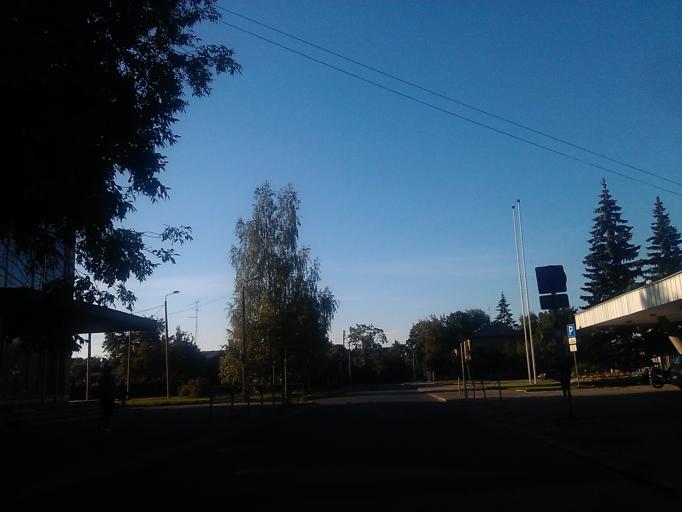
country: LV
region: Riga
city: Jaunciems
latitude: 56.9771
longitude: 24.1940
